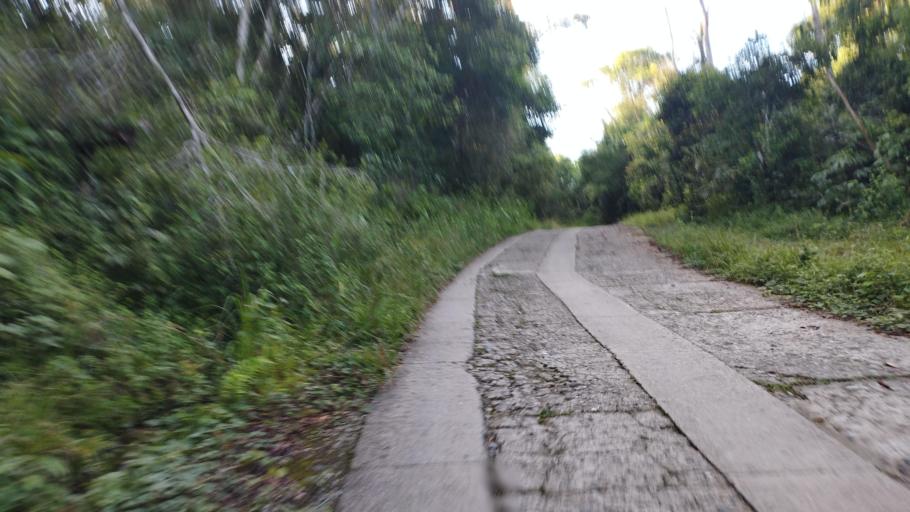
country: CO
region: Casanare
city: Sabanalarga
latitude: 4.8169
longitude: -73.0969
